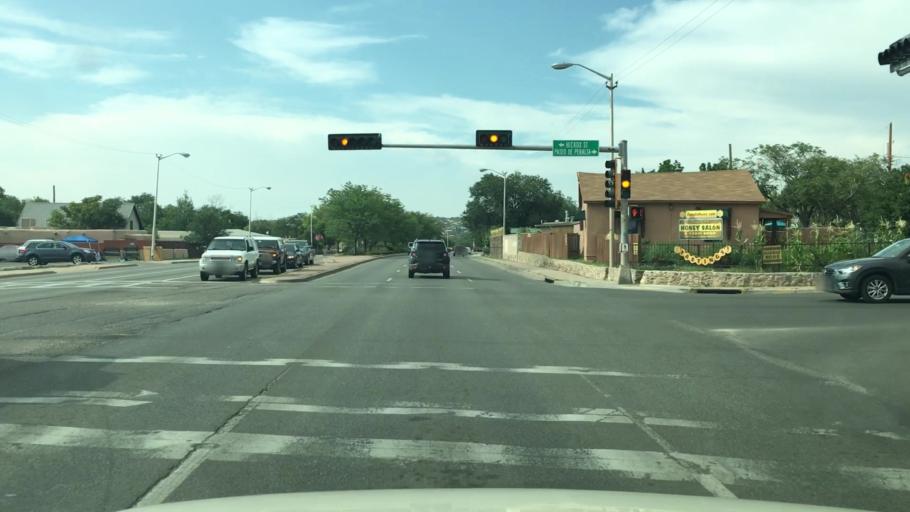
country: US
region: New Mexico
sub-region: Santa Fe County
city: Santa Fe
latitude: 35.6814
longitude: -105.9546
